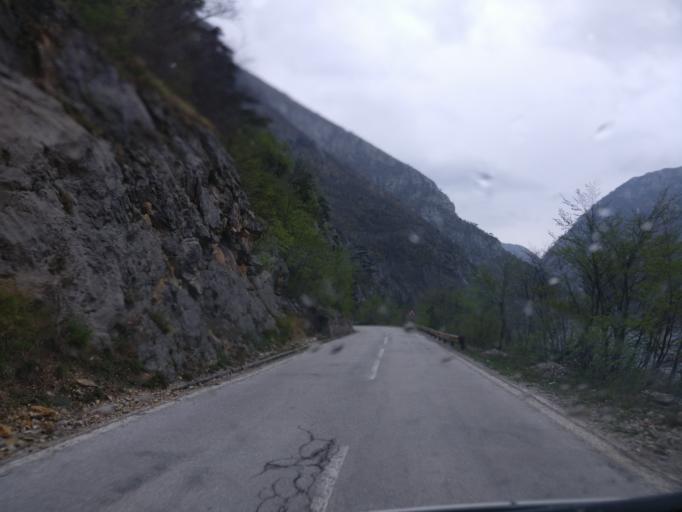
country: ME
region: Opstina Pluzine
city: Pluzine
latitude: 43.2377
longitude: 18.8427
